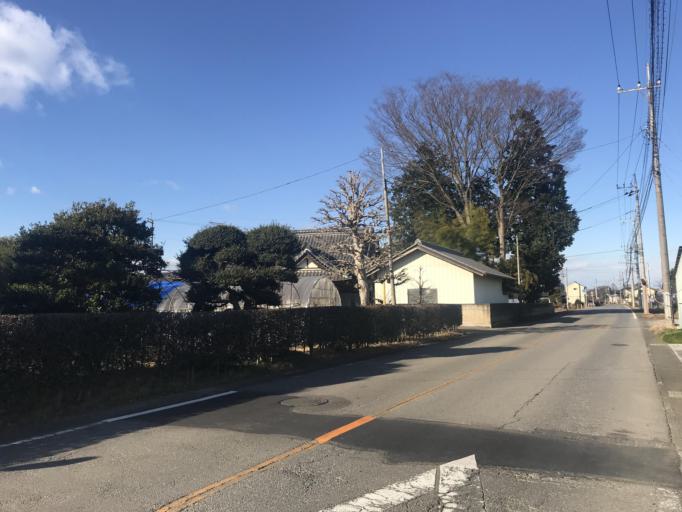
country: JP
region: Tochigi
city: Kaminokawa
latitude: 36.4136
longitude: 139.8775
